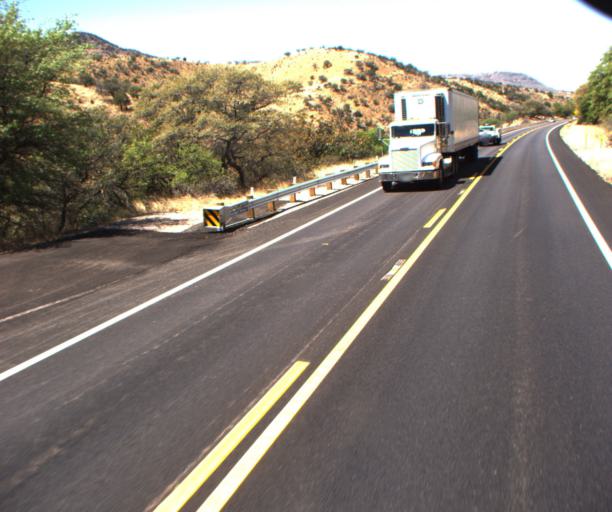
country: US
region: Arizona
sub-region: Cochise County
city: Bisbee
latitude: 31.4757
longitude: -109.9757
